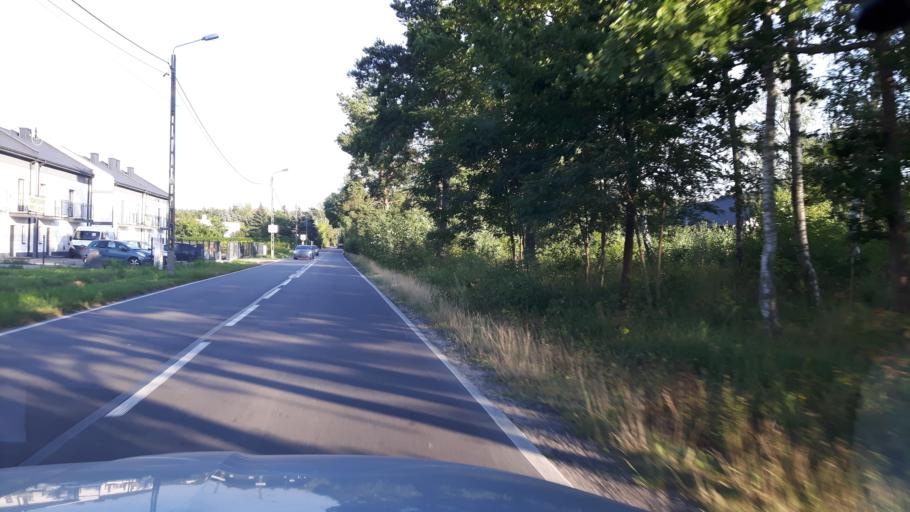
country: PL
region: Masovian Voivodeship
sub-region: Powiat wolominski
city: Kobylka
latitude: 52.3566
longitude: 21.1902
